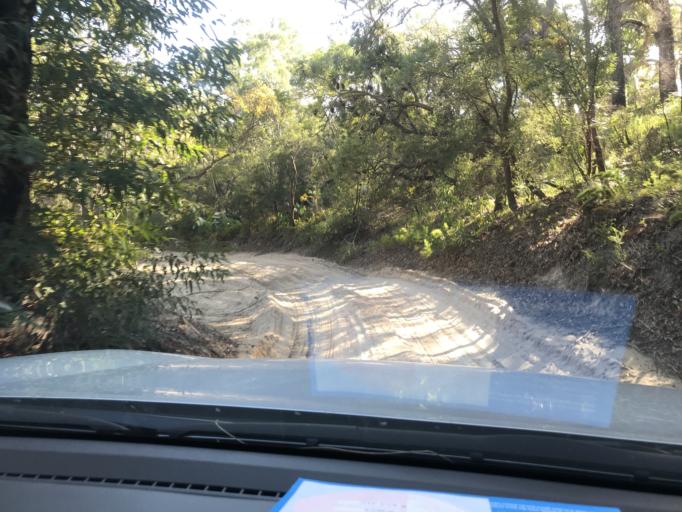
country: AU
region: Queensland
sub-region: Fraser Coast
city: Urangan
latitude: -25.5044
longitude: 153.1090
